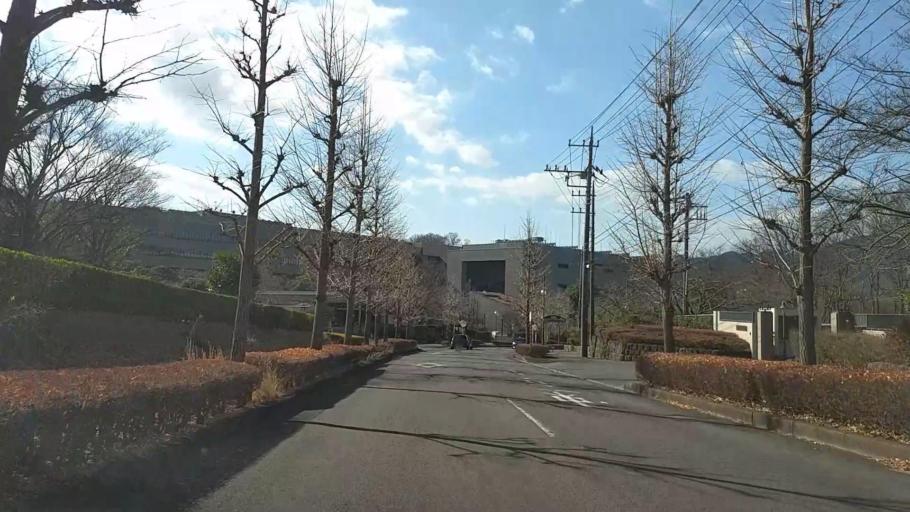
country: JP
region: Kanagawa
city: Atsugi
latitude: 35.4424
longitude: 139.3169
